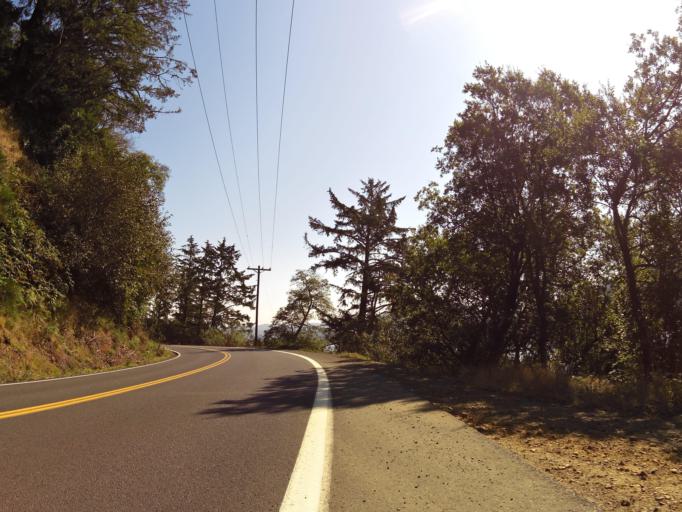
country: US
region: Oregon
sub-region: Tillamook County
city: Pacific City
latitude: 45.1819
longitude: -123.9448
